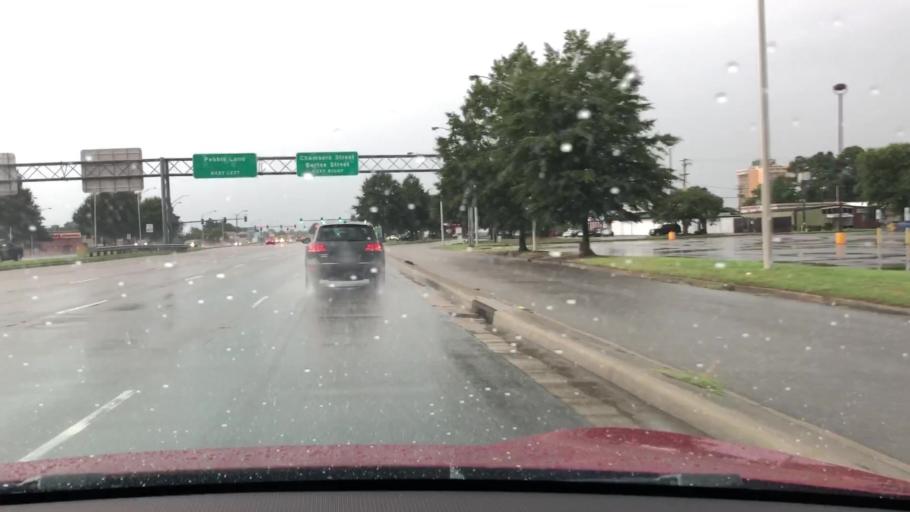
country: US
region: Virginia
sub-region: City of Chesapeake
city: Chesapeake
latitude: 36.8458
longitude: -76.2101
